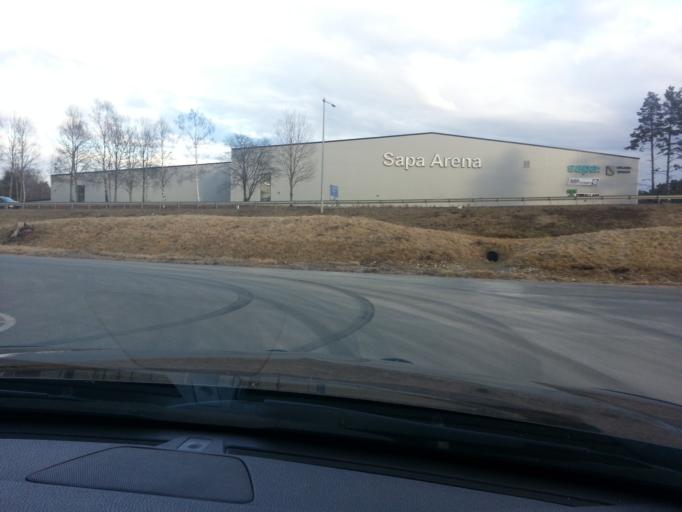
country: SE
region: Joenkoeping
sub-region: Vetlanda Kommun
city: Vetlanda
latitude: 57.4404
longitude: 15.0622
